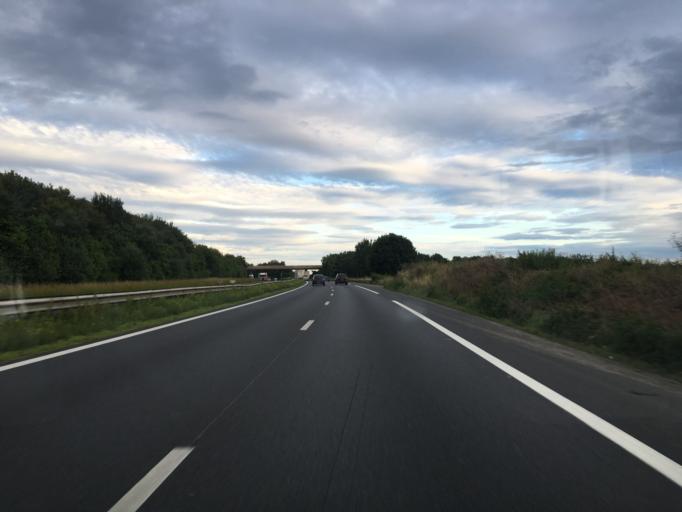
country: FR
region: Ile-de-France
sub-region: Departement de Seine-et-Marne
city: Brie-Comte-Robert
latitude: 48.6872
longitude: 2.5967
